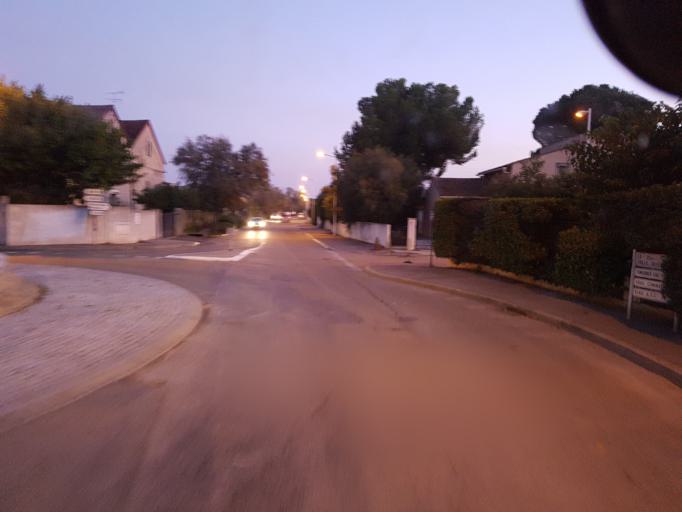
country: FR
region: Languedoc-Roussillon
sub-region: Departement du Gard
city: Bellegarde
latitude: 43.7511
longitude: 4.5177
